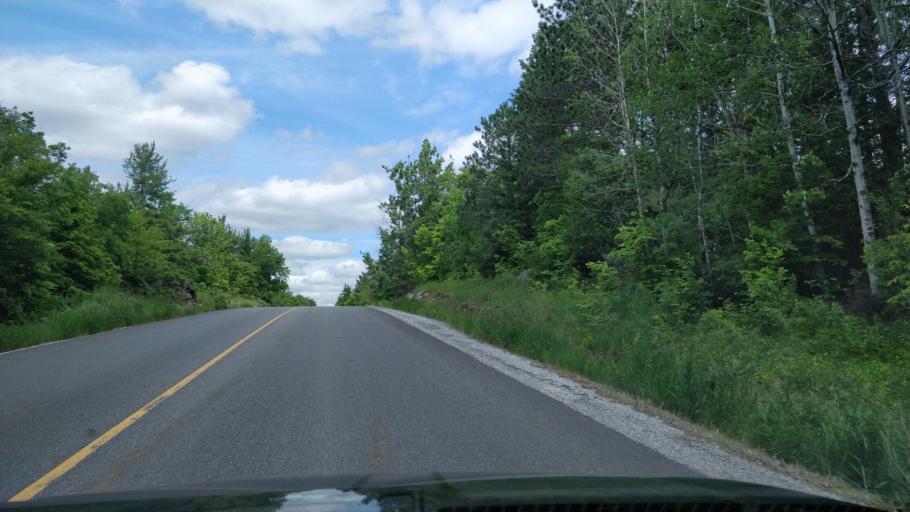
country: CA
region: Ontario
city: Perth
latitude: 44.7804
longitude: -76.4475
